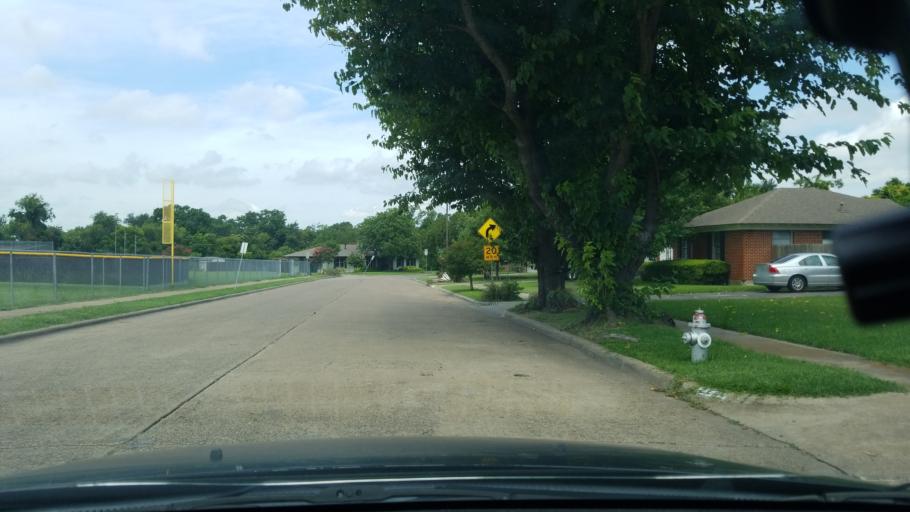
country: US
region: Texas
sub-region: Dallas County
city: Garland
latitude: 32.8289
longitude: -96.6803
